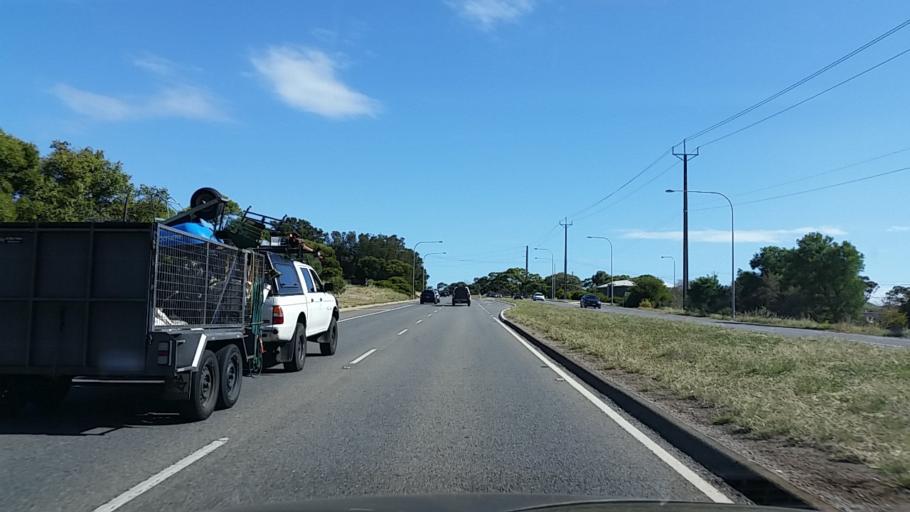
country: AU
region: South Australia
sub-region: Adelaide
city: Port Noarlunga
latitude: -35.1242
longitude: 138.4869
